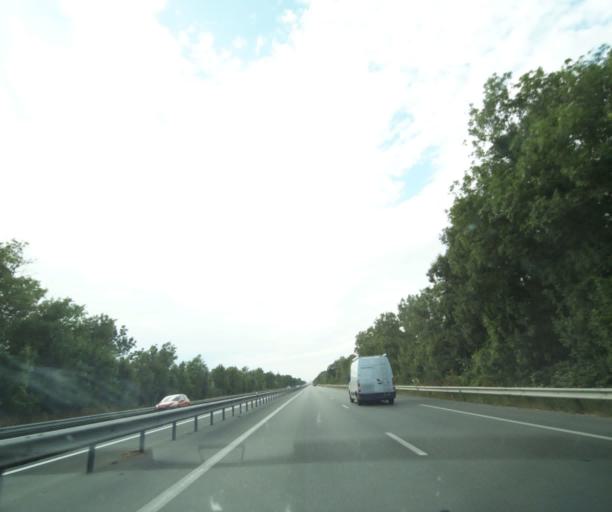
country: FR
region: Poitou-Charentes
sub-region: Departement de la Charente-Maritime
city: Chatelaillon-Plage
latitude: 46.0888
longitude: -1.0831
